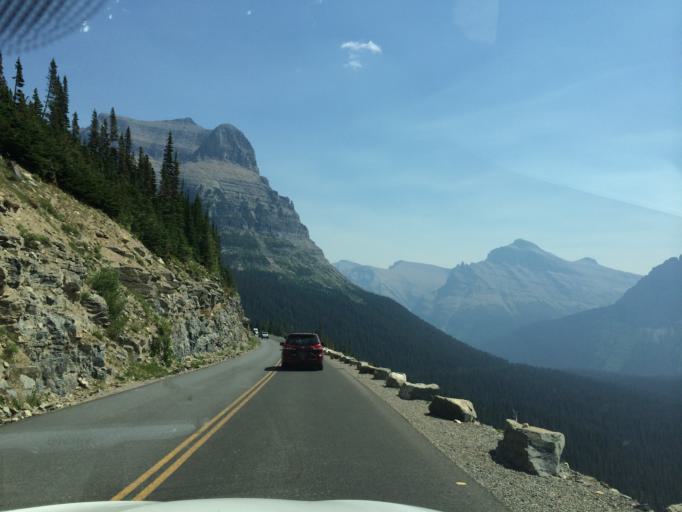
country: US
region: Montana
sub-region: Flathead County
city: Columbia Falls
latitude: 48.6951
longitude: -113.6844
